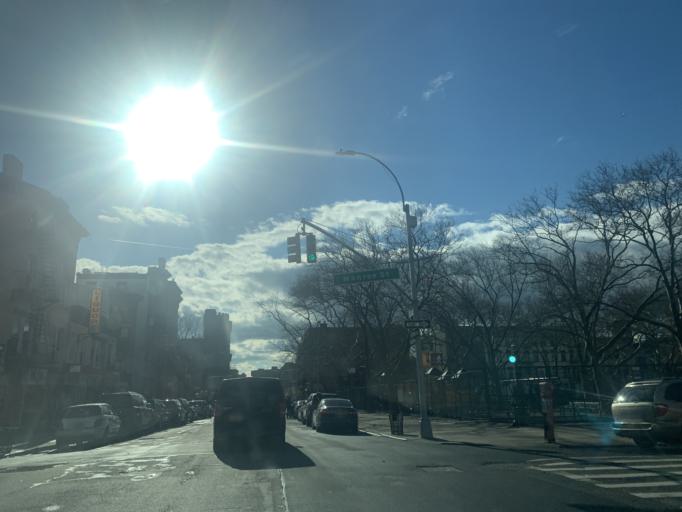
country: US
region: New York
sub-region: Kings County
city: Brooklyn
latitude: 40.6870
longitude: -73.9388
